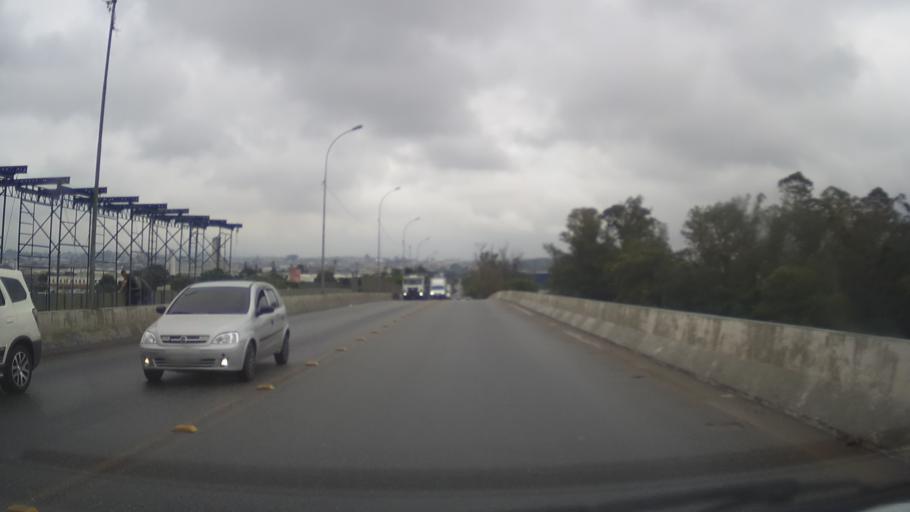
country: BR
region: Sao Paulo
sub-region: Guarulhos
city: Guarulhos
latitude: -23.4811
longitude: -46.4694
